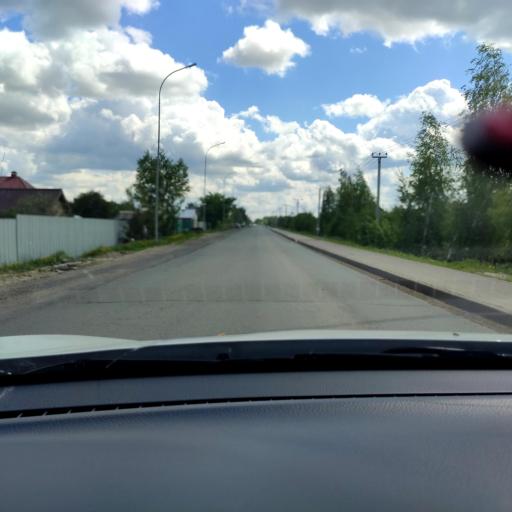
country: RU
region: Tatarstan
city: Stolbishchi
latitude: 55.6982
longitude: 49.1874
